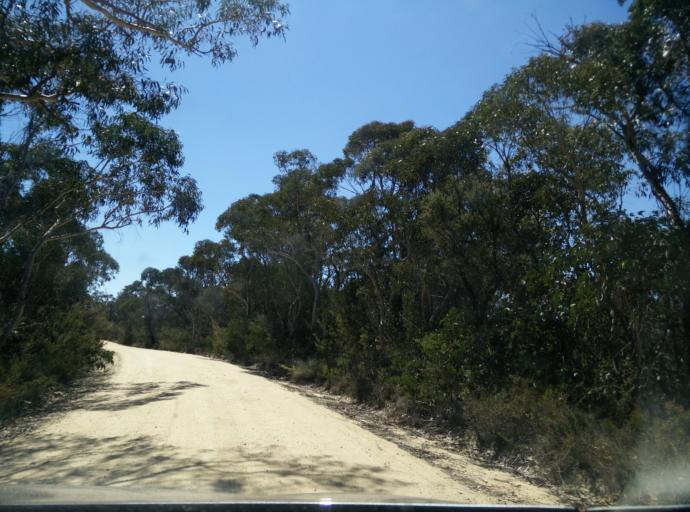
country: AU
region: New South Wales
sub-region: Blue Mountains Municipality
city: Blackheath
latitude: -33.5789
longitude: 150.2769
